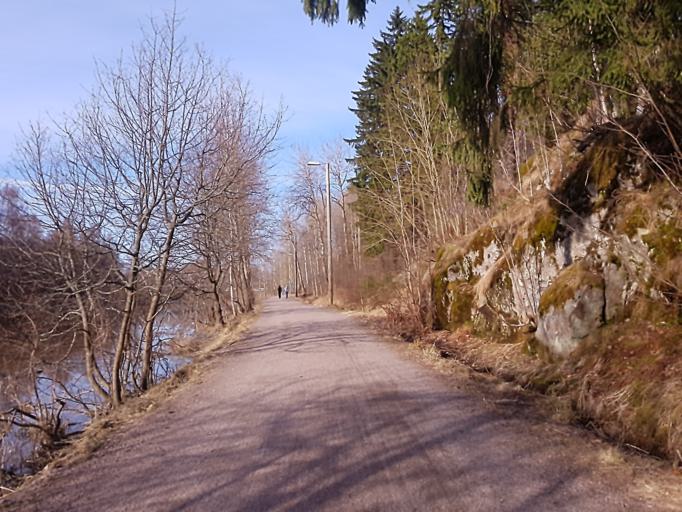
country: FI
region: Uusimaa
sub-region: Helsinki
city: Helsinki
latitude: 60.2289
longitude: 24.9878
